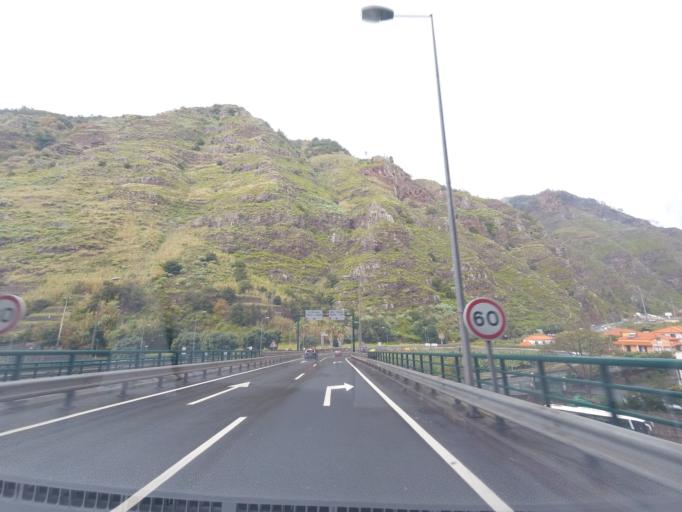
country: PT
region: Madeira
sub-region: Ribeira Brava
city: Campanario
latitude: 32.6737
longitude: -17.0451
